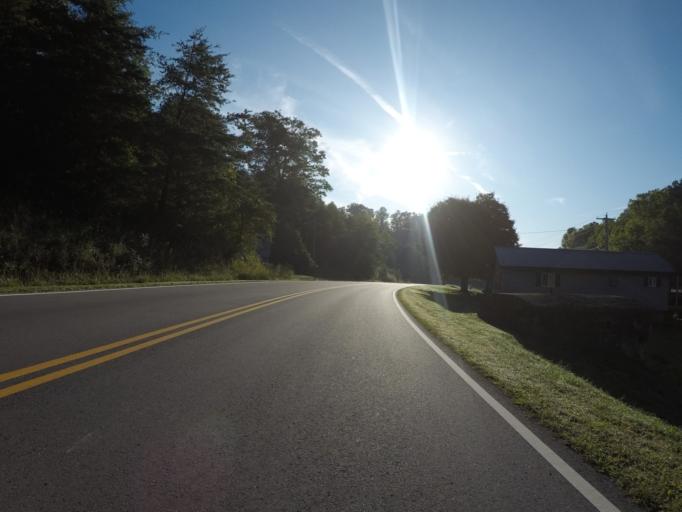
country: US
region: Ohio
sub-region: Lawrence County
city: Coal Grove
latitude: 38.6067
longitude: -82.5781
